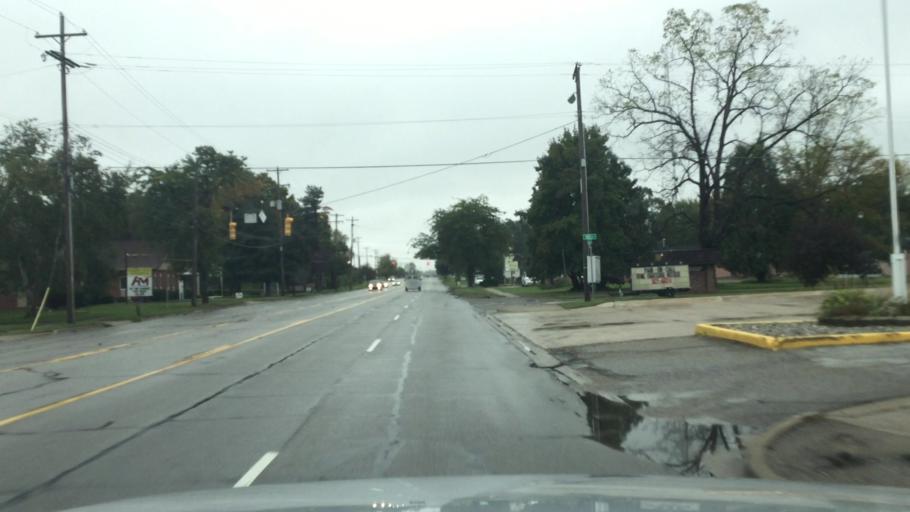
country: US
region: Michigan
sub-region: Saginaw County
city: Bridgeport
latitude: 43.3575
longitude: -83.8794
